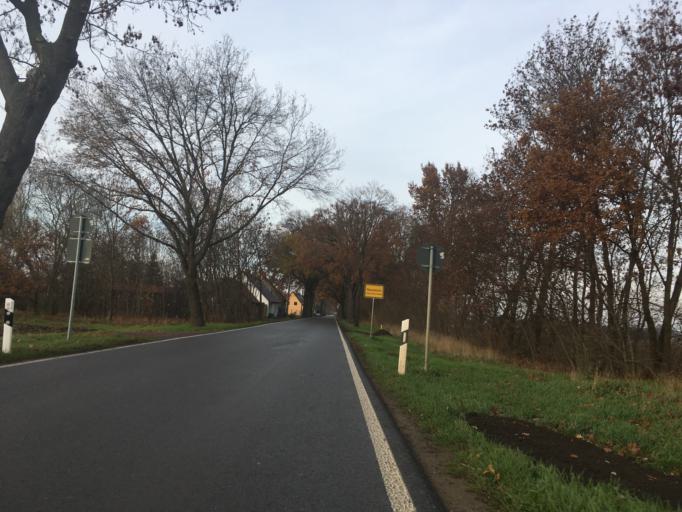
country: DE
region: Brandenburg
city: Neulewin
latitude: 52.7213
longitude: 14.2864
